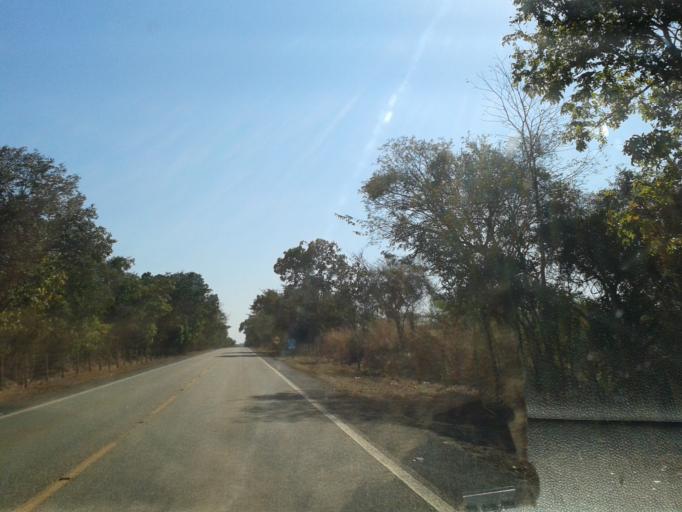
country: BR
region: Goias
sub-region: Mozarlandia
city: Mozarlandia
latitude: -14.6725
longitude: -50.5351
